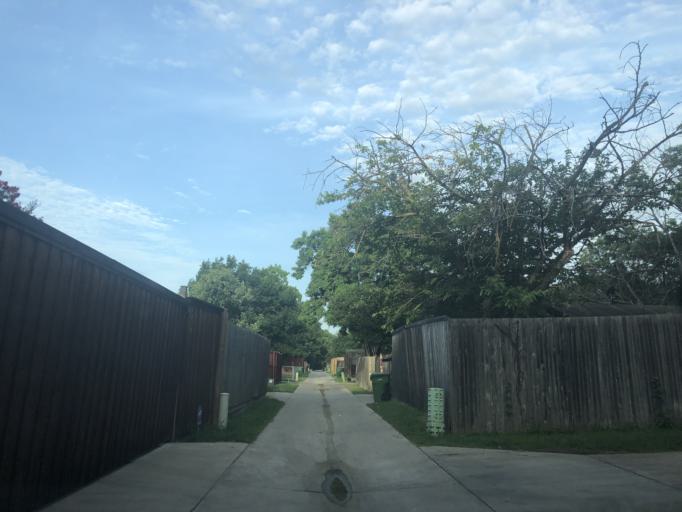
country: US
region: Texas
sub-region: Dallas County
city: Sunnyvale
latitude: 32.8402
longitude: -96.5880
